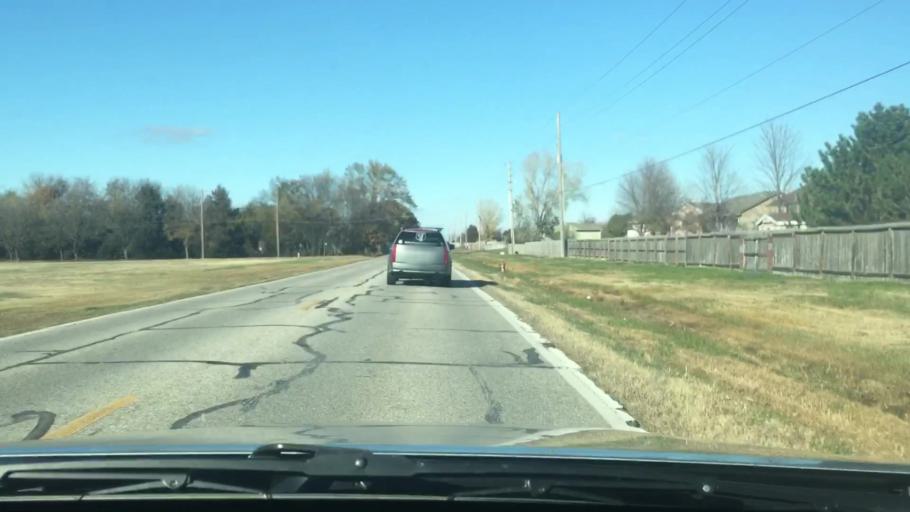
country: US
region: Kansas
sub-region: Sedgwick County
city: Maize
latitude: 37.7284
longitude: -97.4810
